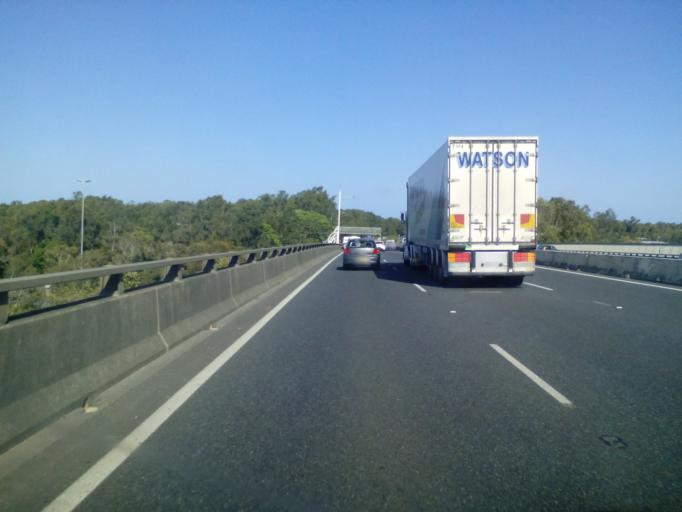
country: AU
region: New South Wales
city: Chinderah
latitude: -28.2250
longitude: 153.5558
